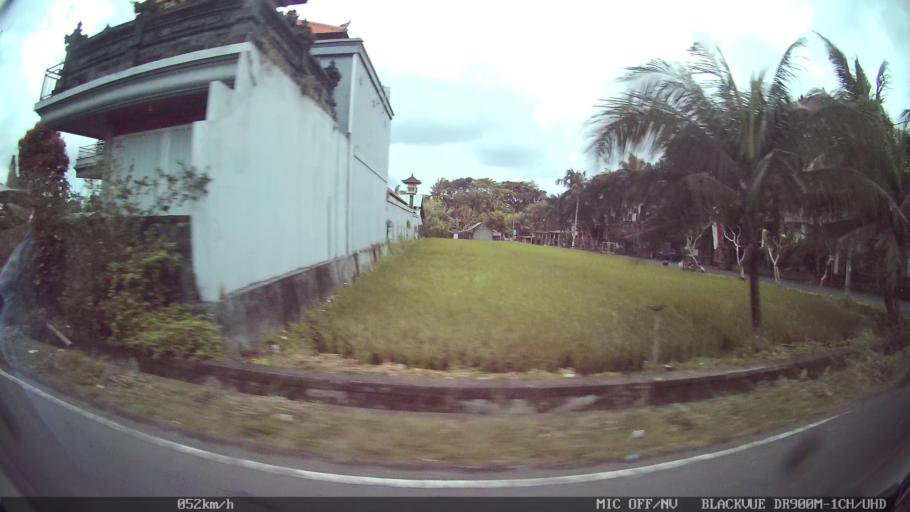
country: ID
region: Bali
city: Banjar Serangan
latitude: -8.5553
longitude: 115.1803
